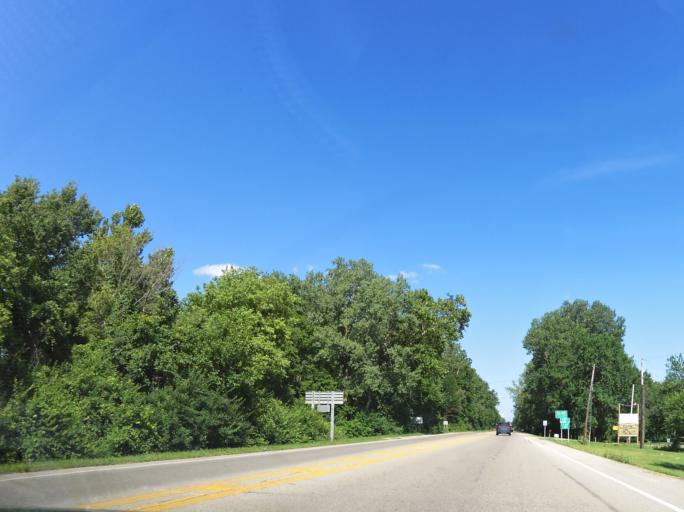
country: US
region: Ohio
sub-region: Greene County
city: Wright-Patterson AFB
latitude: 39.8435
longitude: -84.0553
